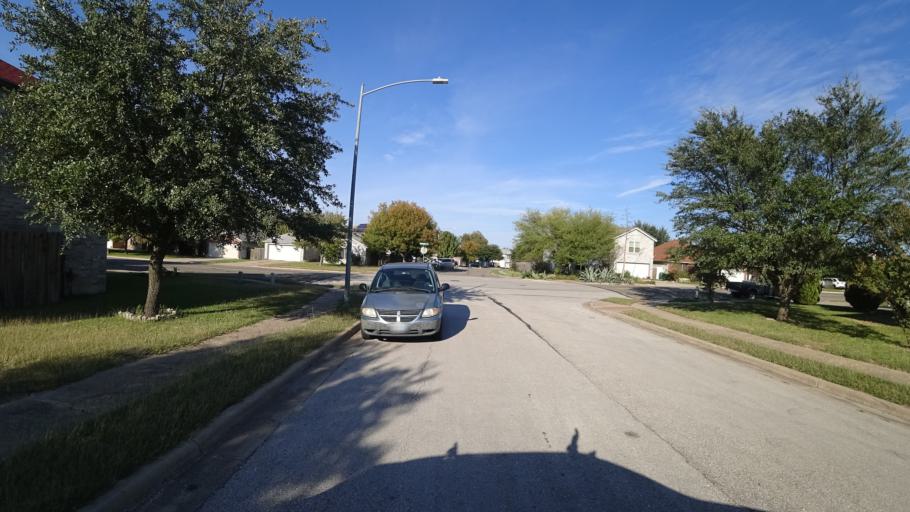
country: US
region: Texas
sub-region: Travis County
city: Pflugerville
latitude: 30.3973
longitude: -97.6513
